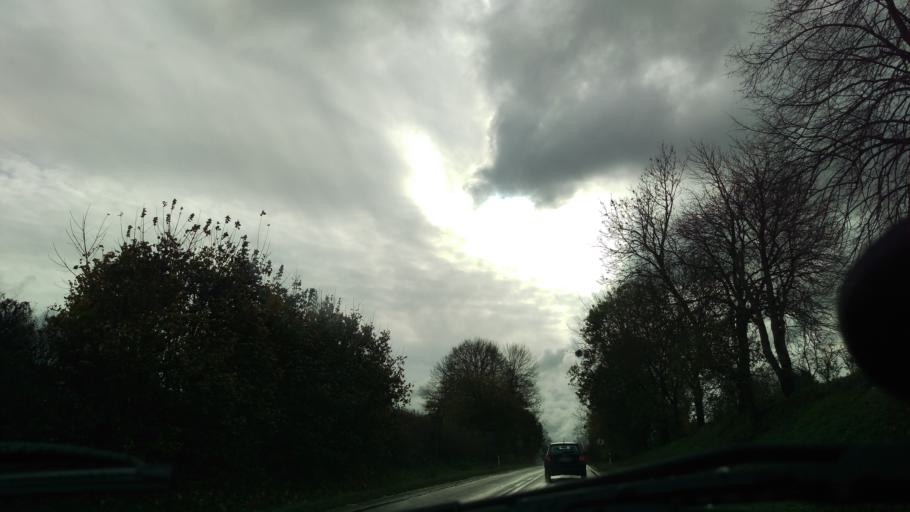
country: PL
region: West Pomeranian Voivodeship
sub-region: Powiat gryficki
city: Gryfice
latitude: 53.9037
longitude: 15.2021
